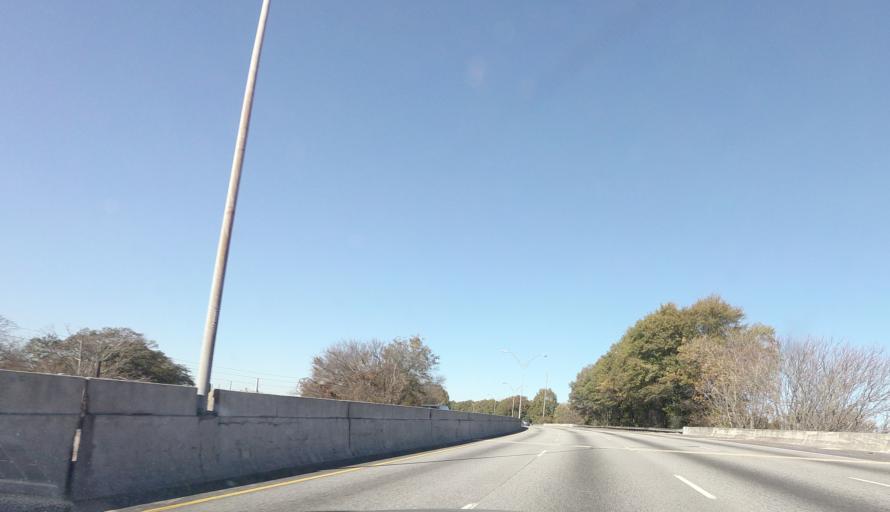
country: US
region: Georgia
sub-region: Fulton County
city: Atlanta
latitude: 33.7509
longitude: -84.4445
